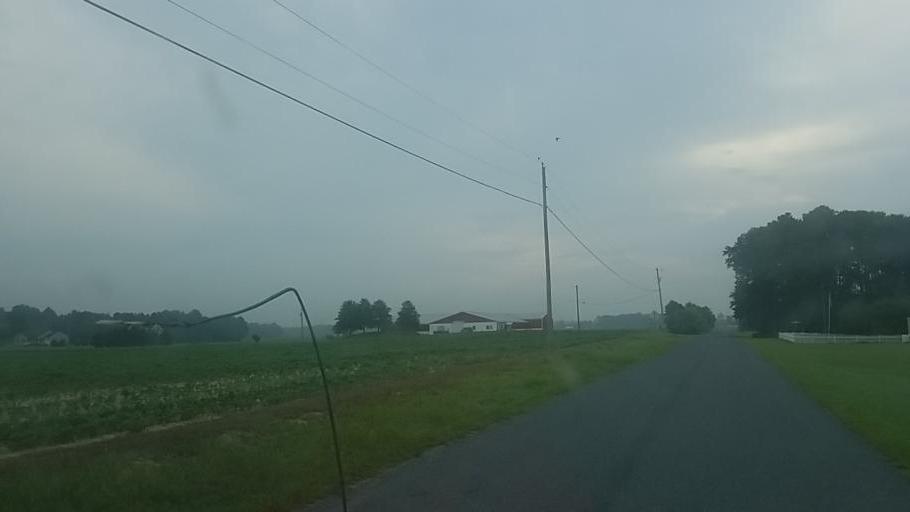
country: US
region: Maryland
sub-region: Wicomico County
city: Pittsville
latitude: 38.4521
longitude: -75.3698
